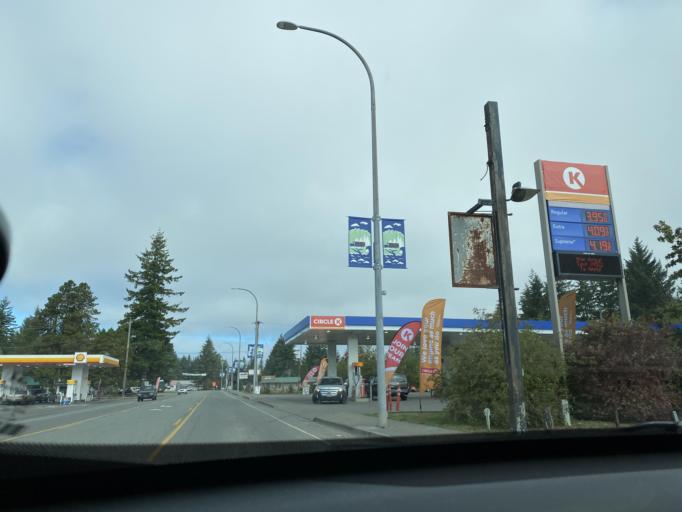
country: US
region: Washington
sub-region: Clallam County
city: Forks
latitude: 47.9520
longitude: -124.3853
